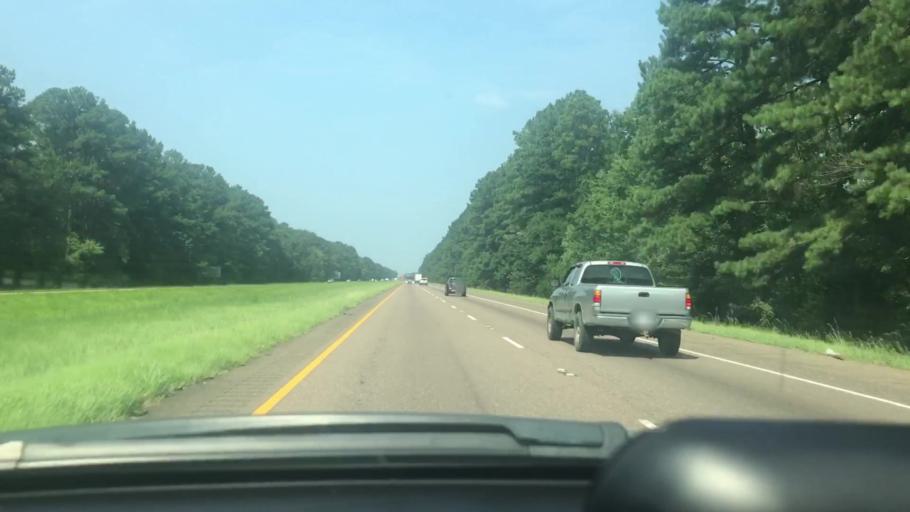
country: US
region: Louisiana
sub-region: Livingston Parish
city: Livingston
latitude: 30.4742
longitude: -90.7629
